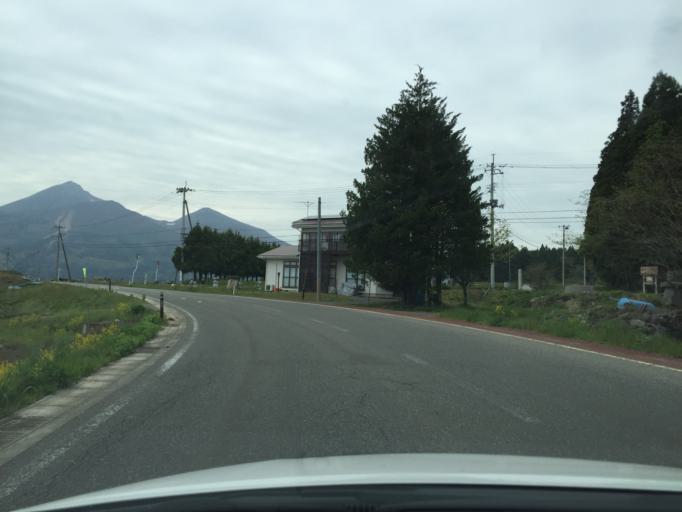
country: JP
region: Fukushima
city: Inawashiro
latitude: 37.5577
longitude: 140.1386
